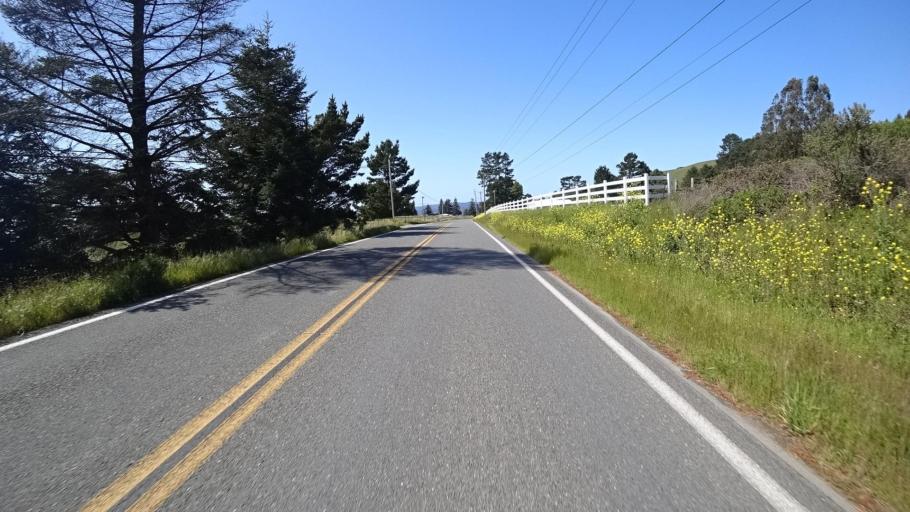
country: US
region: California
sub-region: Humboldt County
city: Hydesville
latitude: 40.5530
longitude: -124.1204
